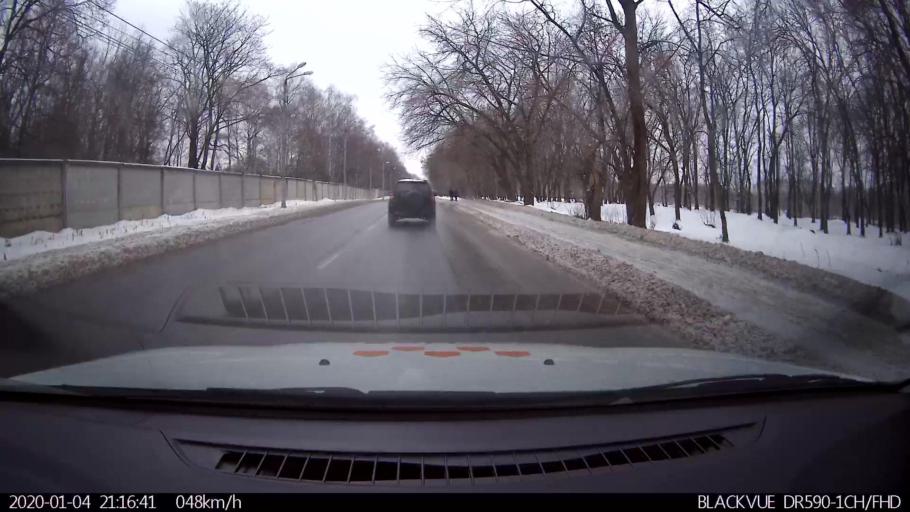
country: RU
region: Nizjnij Novgorod
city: Gorbatovka
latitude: 56.2392
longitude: 43.8494
